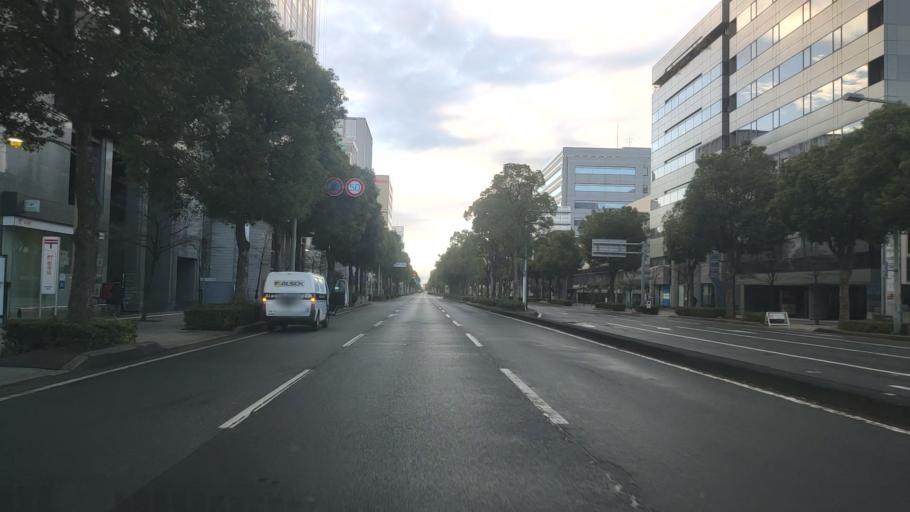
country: JP
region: Hyogo
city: Himeji
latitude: 34.8252
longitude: 134.6891
